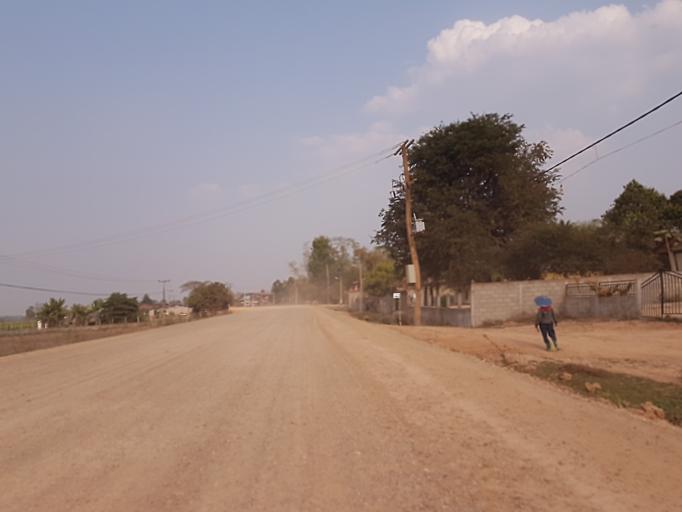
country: TH
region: Nong Khai
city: Nong Khai
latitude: 17.9814
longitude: 102.8846
